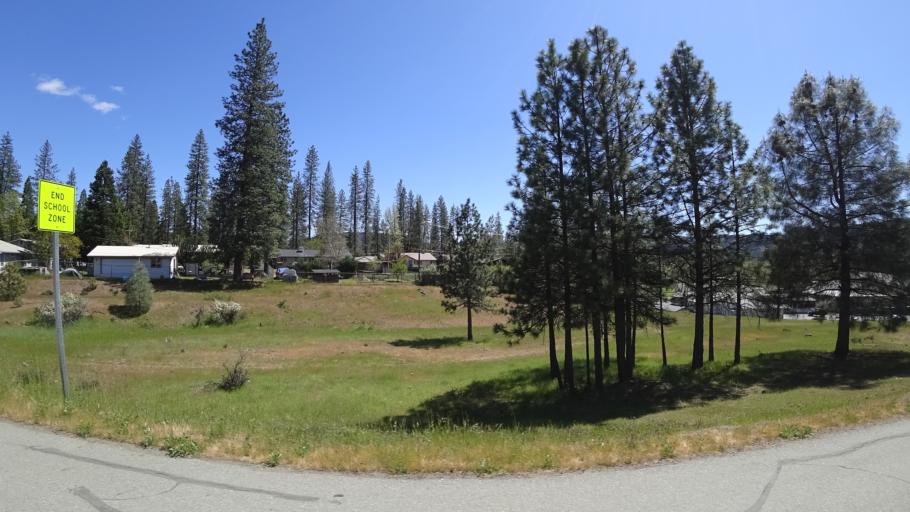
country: US
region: California
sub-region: Trinity County
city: Weaverville
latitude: 40.7341
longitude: -122.9347
